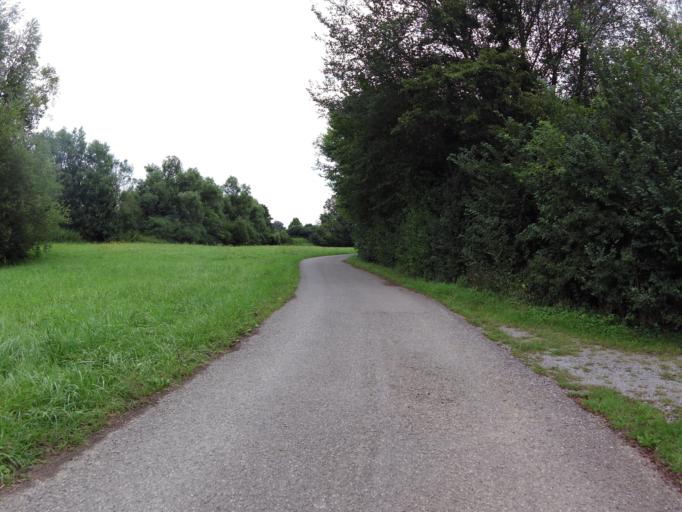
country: DE
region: Bavaria
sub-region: Regierungsbezirk Unterfranken
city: Wonfurt
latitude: 50.0185
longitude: 10.4574
